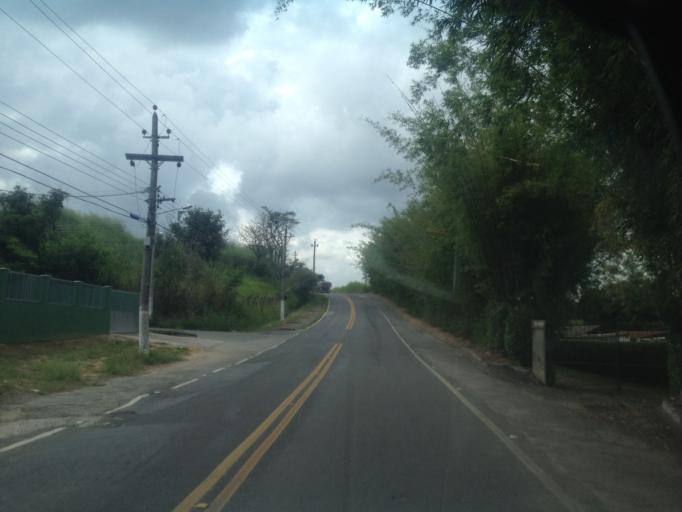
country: BR
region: Rio de Janeiro
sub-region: Quatis
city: Quatis
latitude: -22.4139
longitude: -44.2731
